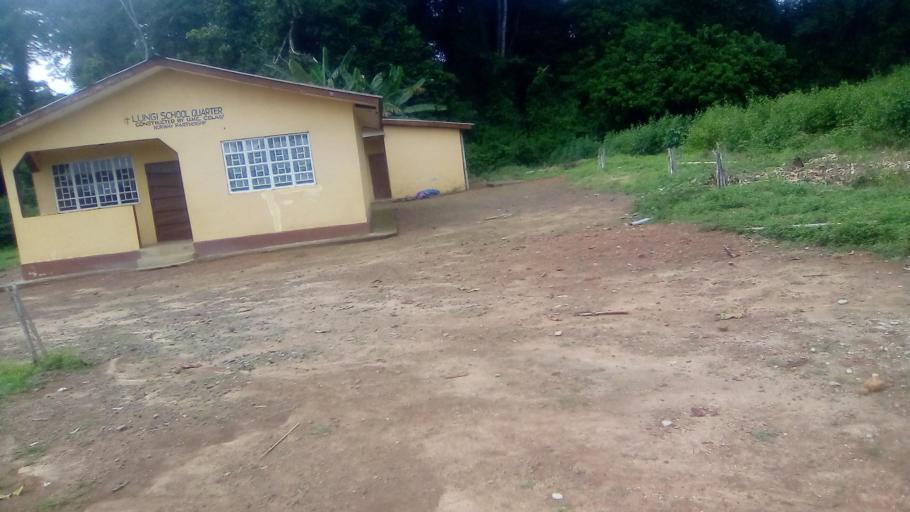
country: SL
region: Southern Province
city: Moyamba
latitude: 8.1365
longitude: -12.4050
